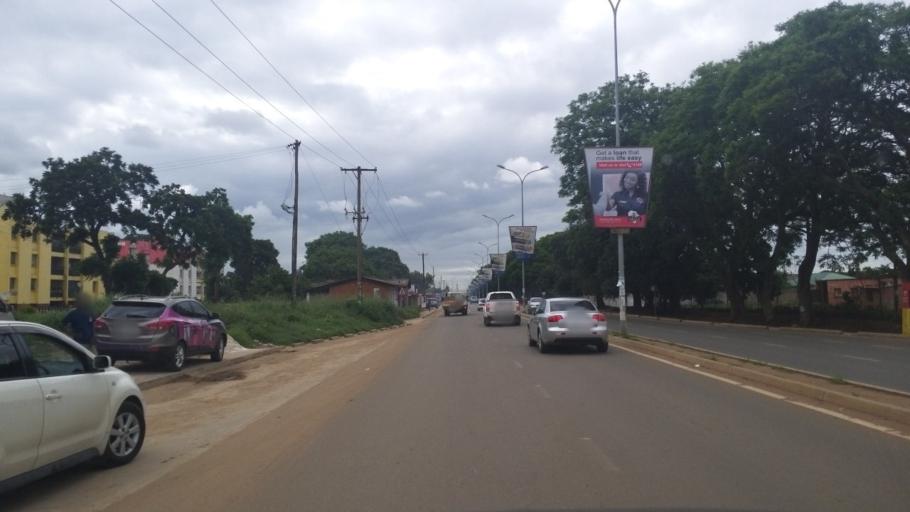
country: ZM
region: Lusaka
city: Lusaka
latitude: -15.4337
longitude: 28.3071
